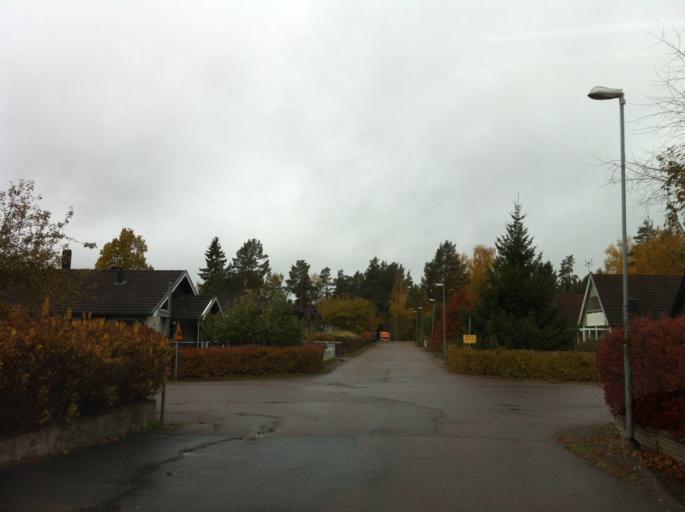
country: SE
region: Uppsala
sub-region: Osthammars Kommun
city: OEsthammar
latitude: 60.2699
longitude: 18.3639
